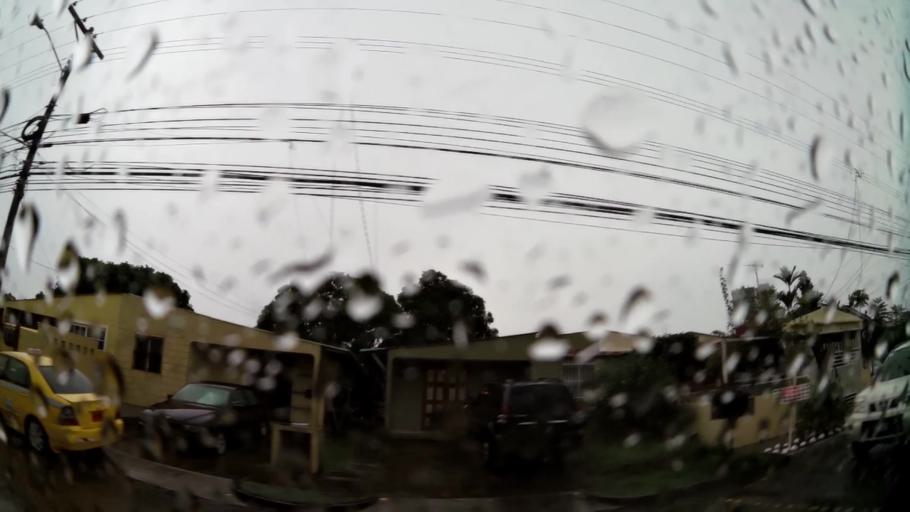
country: PA
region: Panama
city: San Miguelito
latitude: 9.0510
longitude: -79.4744
